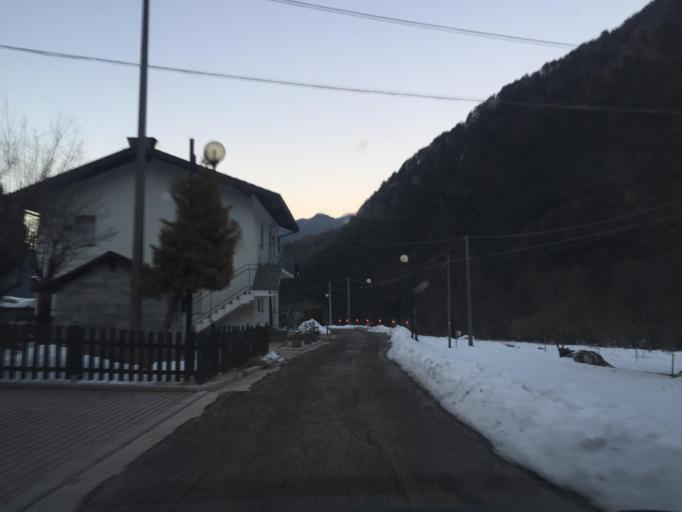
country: IT
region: Friuli Venezia Giulia
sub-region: Provincia di Udine
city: Prato
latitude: 46.3527
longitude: 13.2937
